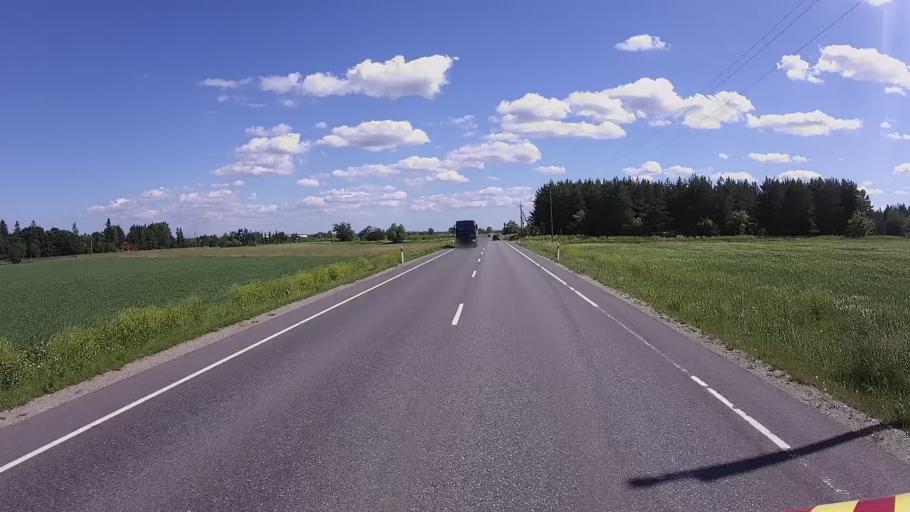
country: EE
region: Ida-Virumaa
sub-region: Johvi vald
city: Johvi
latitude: 59.3352
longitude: 27.3707
